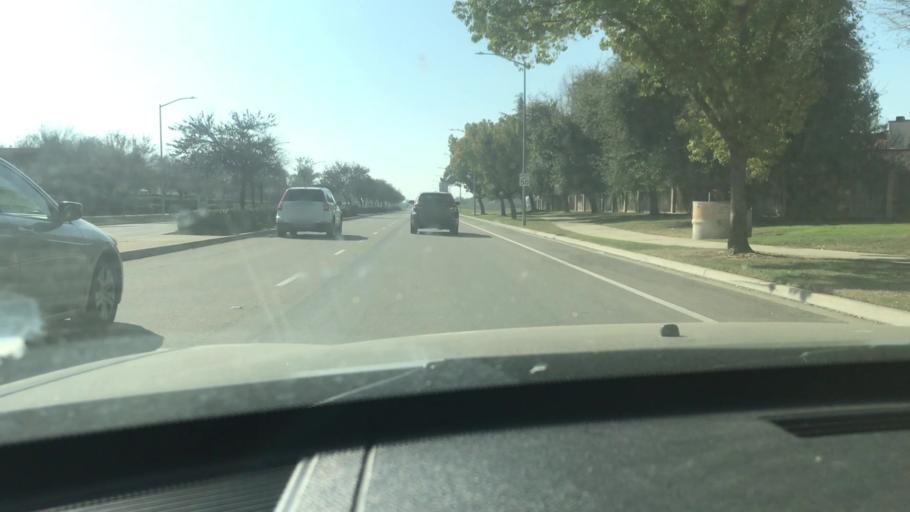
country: US
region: California
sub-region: Fresno County
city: Tarpey Village
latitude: 36.7933
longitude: -119.6641
